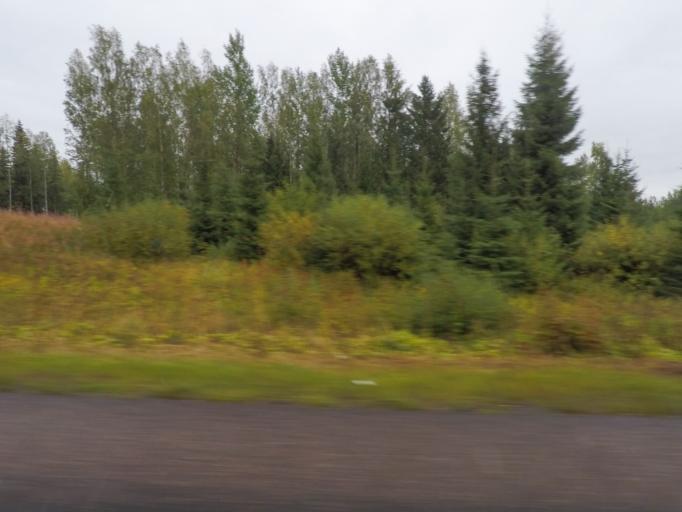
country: FI
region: Northern Savo
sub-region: Varkaus
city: Leppaevirta
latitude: 62.4563
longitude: 27.7866
